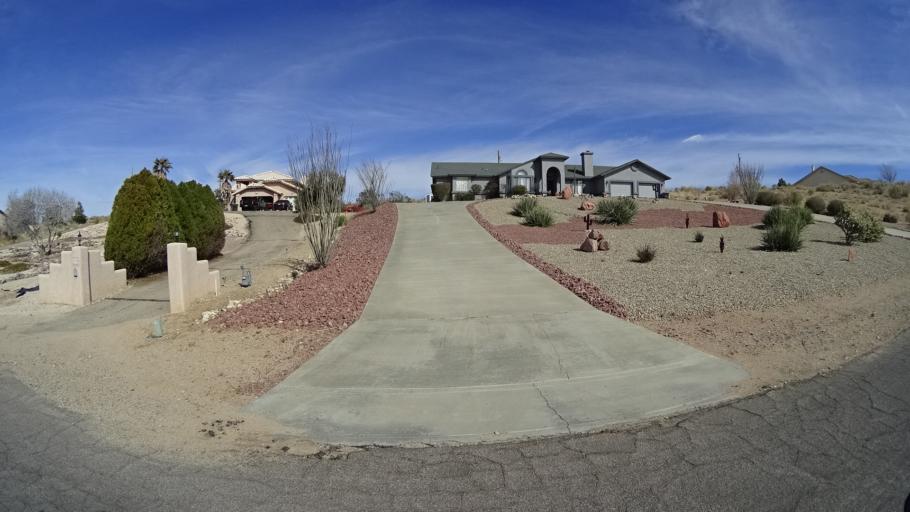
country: US
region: Arizona
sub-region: Mohave County
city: Kingman
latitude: 35.1801
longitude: -113.9895
